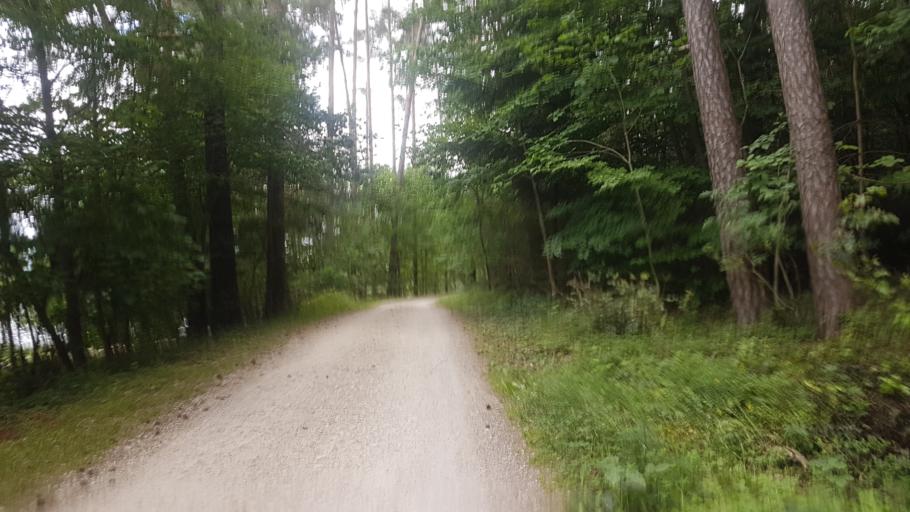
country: DE
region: Bavaria
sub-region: Regierungsbezirk Mittelfranken
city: Pleinfeld
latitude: 49.1188
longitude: 10.9474
